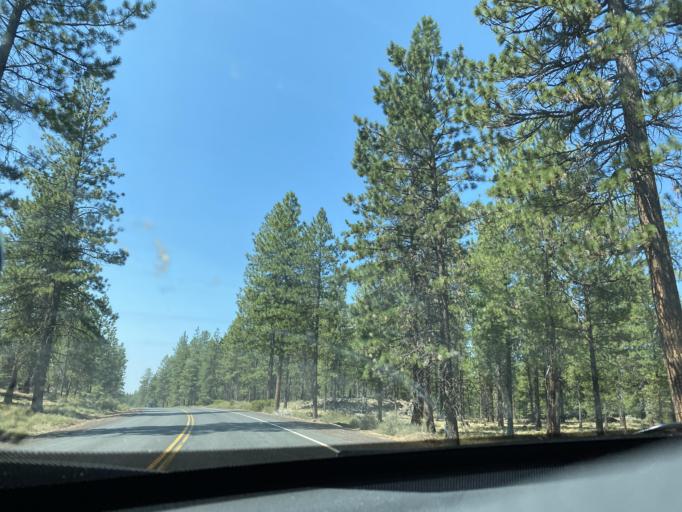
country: US
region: Oregon
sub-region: Deschutes County
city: Sunriver
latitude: 43.8911
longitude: -121.3867
